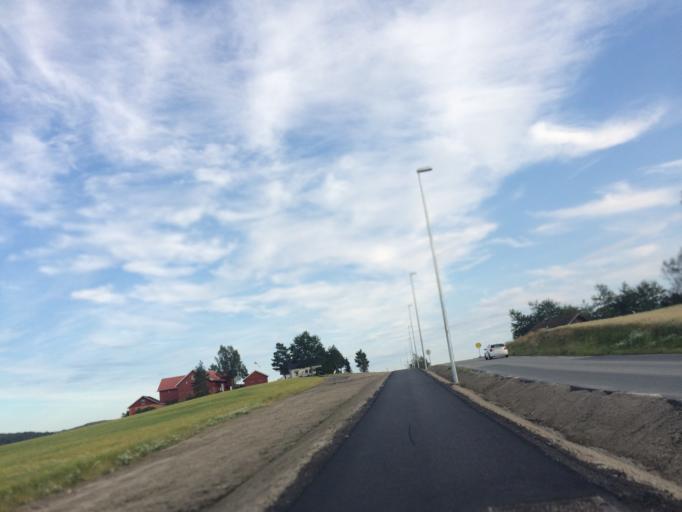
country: NO
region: Akershus
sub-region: Ski
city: Ski
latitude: 59.6944
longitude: 10.8594
